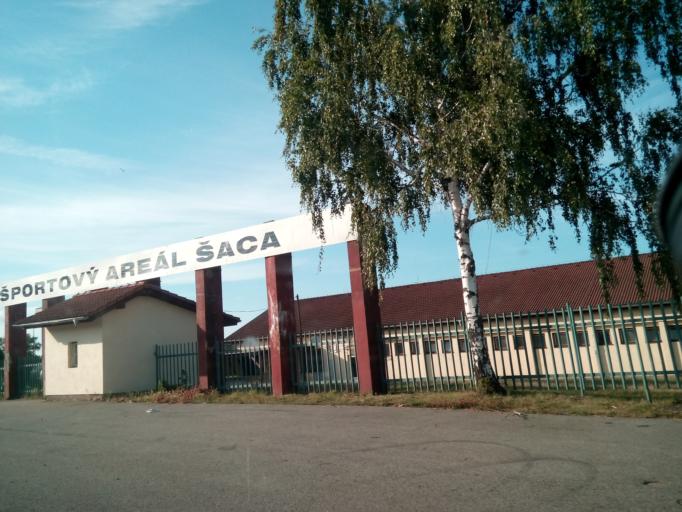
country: SK
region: Kosicky
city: Kosice
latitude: 48.6349
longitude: 21.1760
